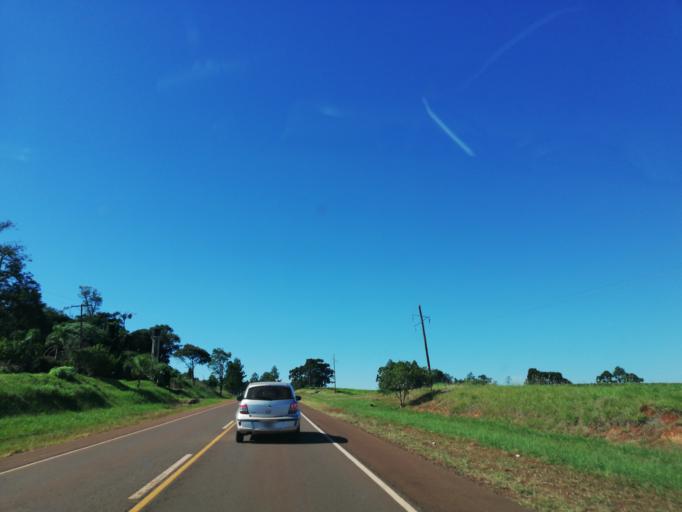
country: AR
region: Misiones
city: Dos de Mayo
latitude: -27.0667
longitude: -54.4176
